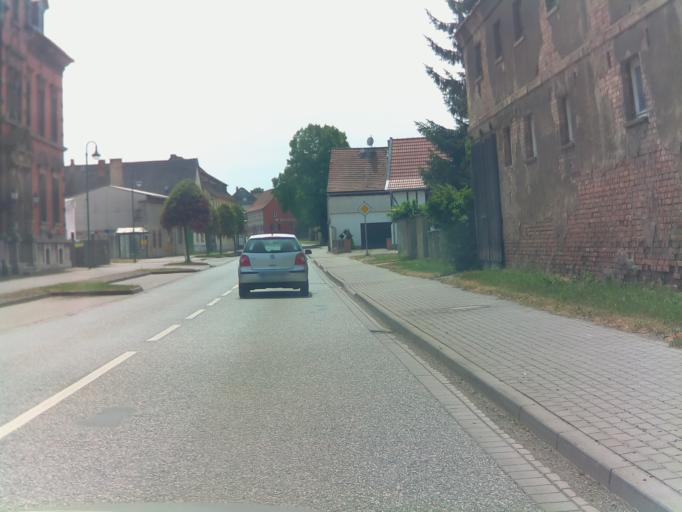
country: DE
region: Saxony-Anhalt
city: Hedersleben
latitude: 51.8415
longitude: 11.2453
